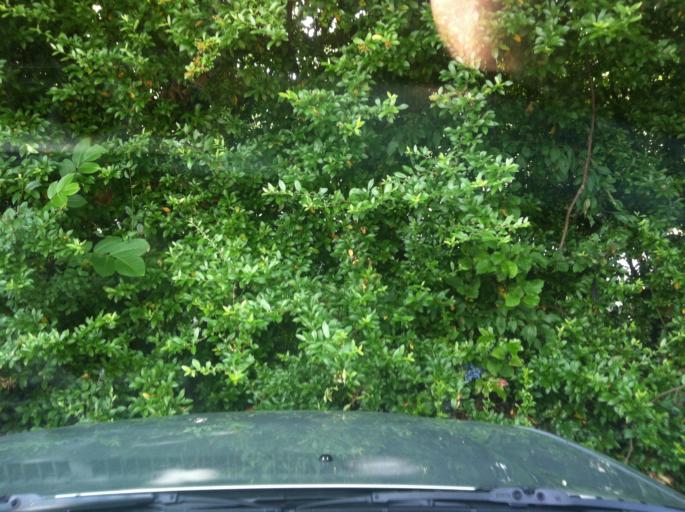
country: DE
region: North Rhine-Westphalia
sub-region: Regierungsbezirk Koln
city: Porz am Rhein
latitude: 50.8653
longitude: 7.0367
